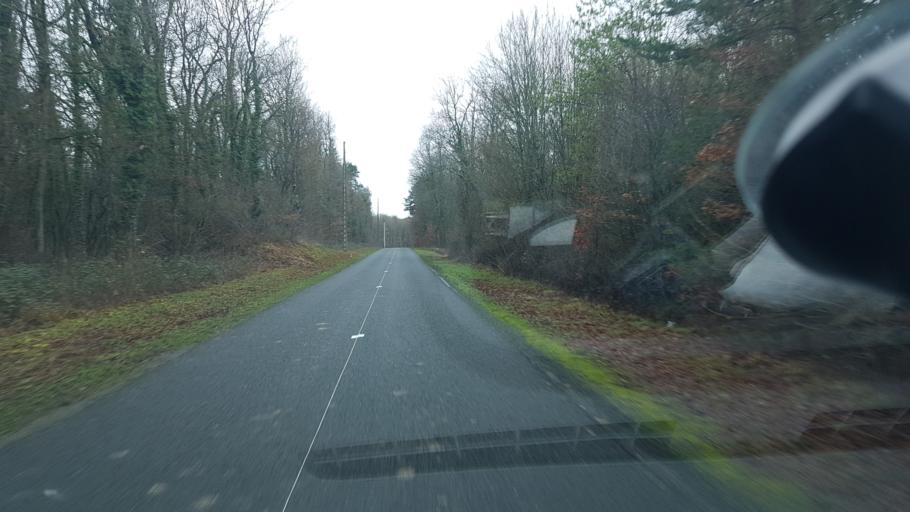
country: FR
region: Ile-de-France
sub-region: Departement de Seine-et-Marne
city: Montigny-sur-Loing
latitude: 48.2759
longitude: 2.7803
